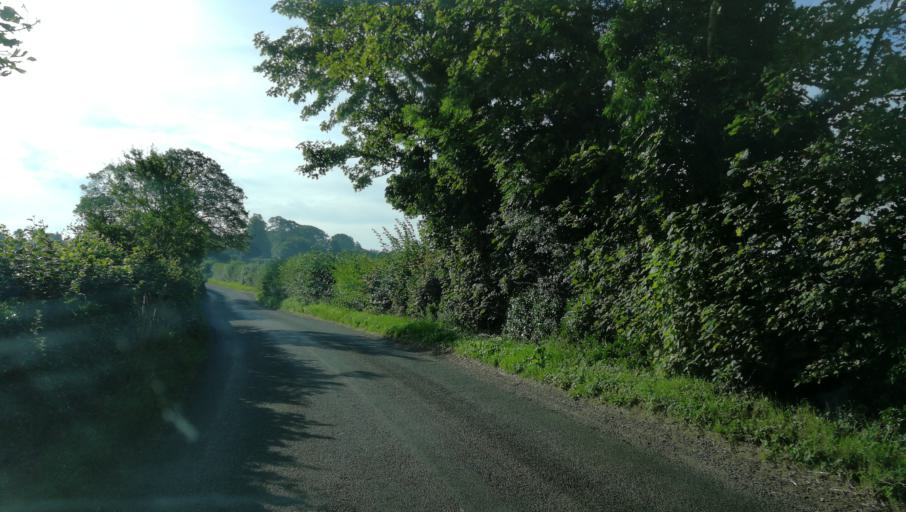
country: GB
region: England
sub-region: Oxfordshire
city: Bloxham
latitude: 52.0310
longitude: -1.4085
